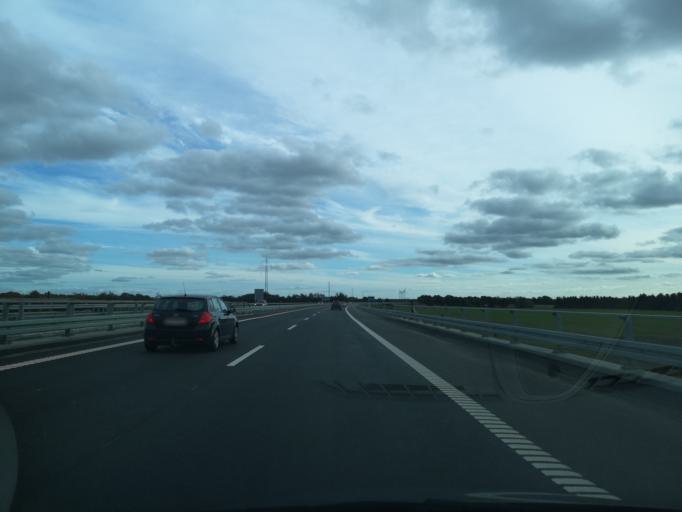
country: DK
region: Central Jutland
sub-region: Holstebro Kommune
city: Holstebro
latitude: 56.3638
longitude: 8.7269
